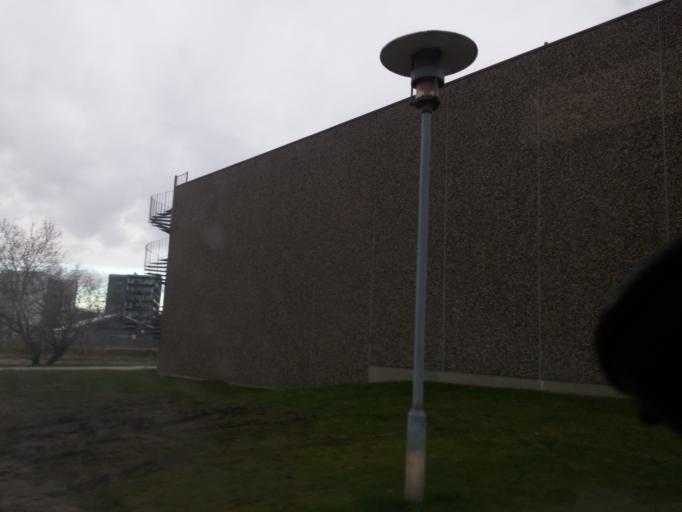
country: DK
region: South Denmark
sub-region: Odense Kommune
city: Odense
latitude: 55.4048
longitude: 10.3808
